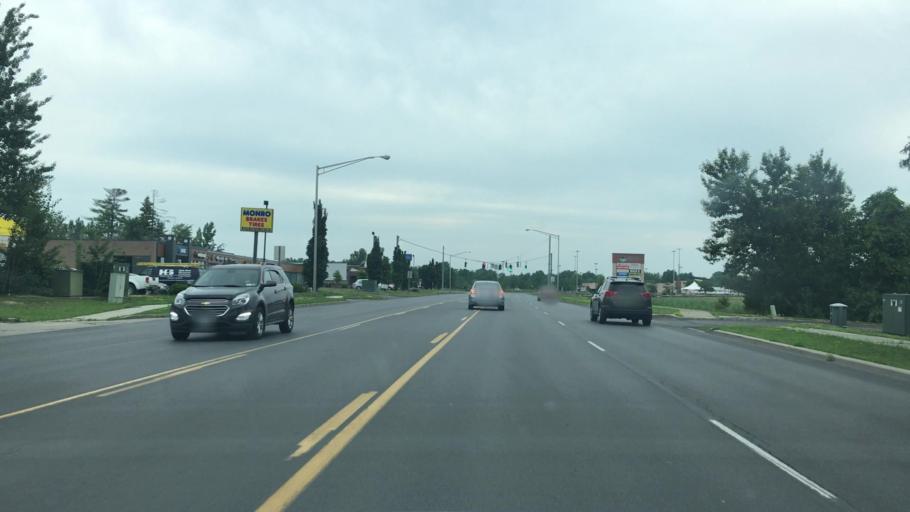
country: US
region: New York
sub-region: Clinton County
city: Plattsburgh West
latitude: 44.6987
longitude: -73.4935
